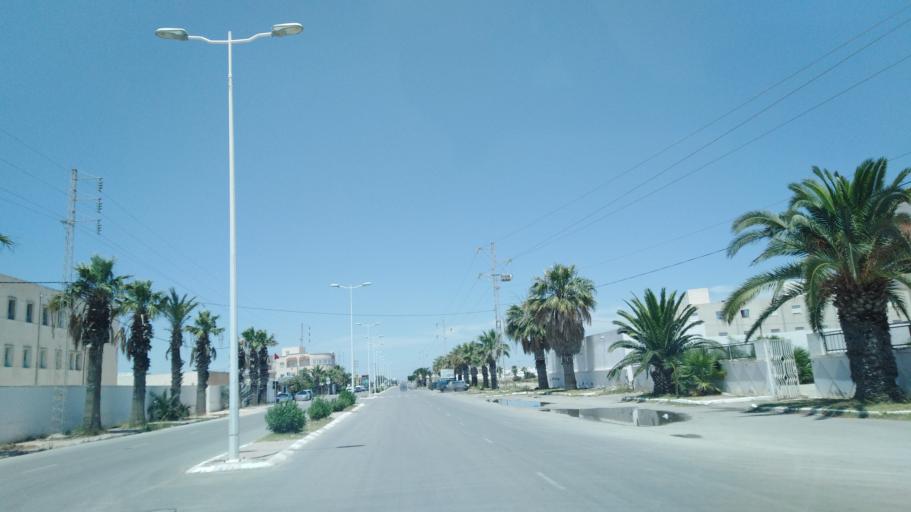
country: TN
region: Al Mahdiyah
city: Ksour Essaf
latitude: 35.4247
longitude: 10.9959
